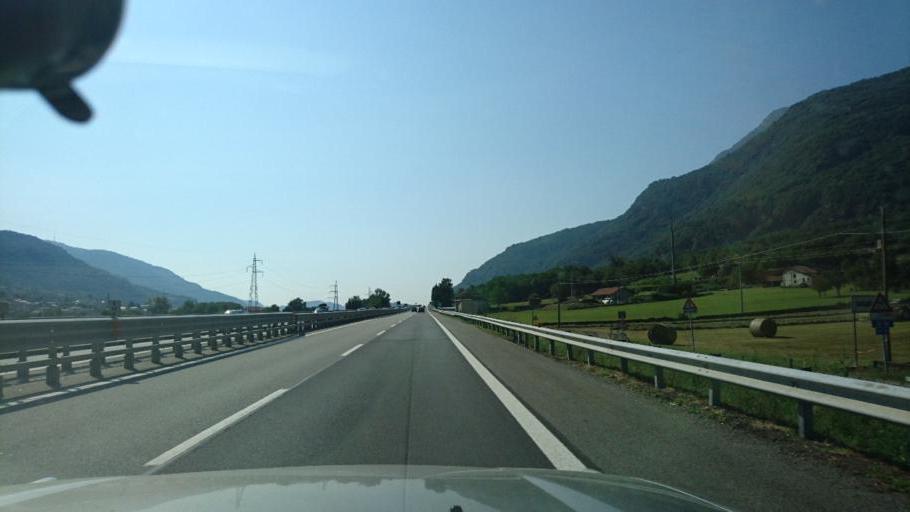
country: IT
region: Piedmont
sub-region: Provincia di Torino
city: Quincinetto
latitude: 45.5562
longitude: 7.8182
